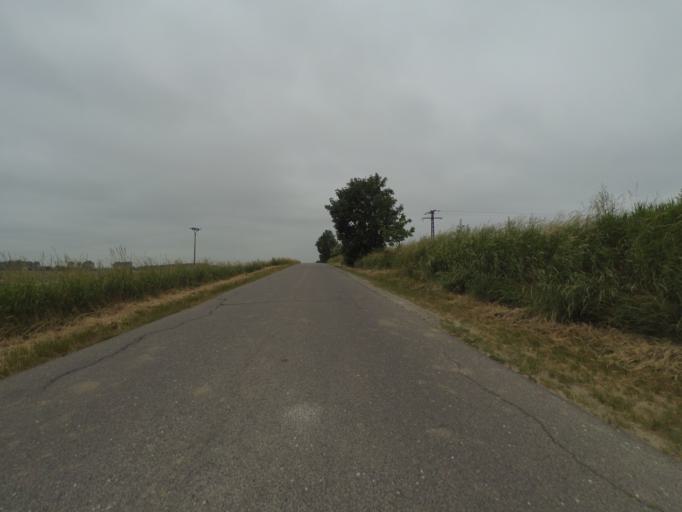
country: DE
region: Mecklenburg-Vorpommern
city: Dobbertin
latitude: 53.5861
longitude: 12.0276
